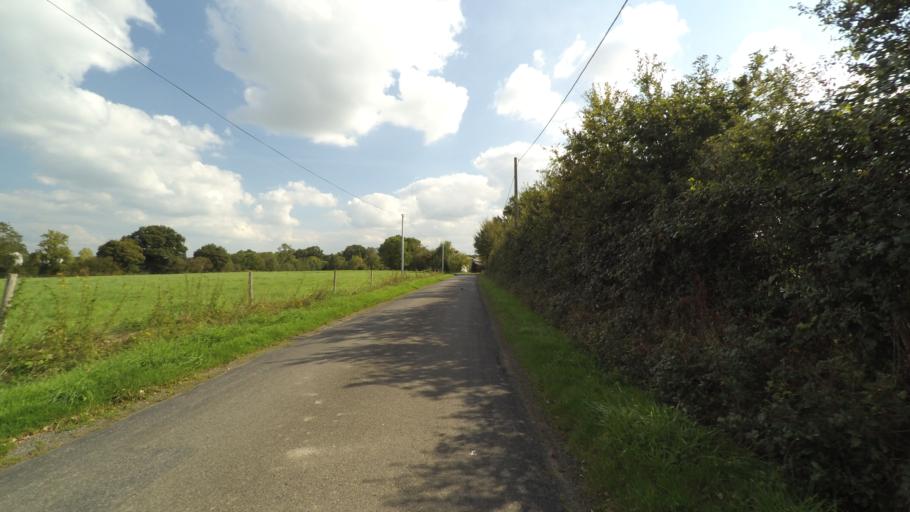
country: FR
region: Pays de la Loire
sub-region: Departement de la Vendee
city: Bouffere
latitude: 46.9538
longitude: -1.3752
